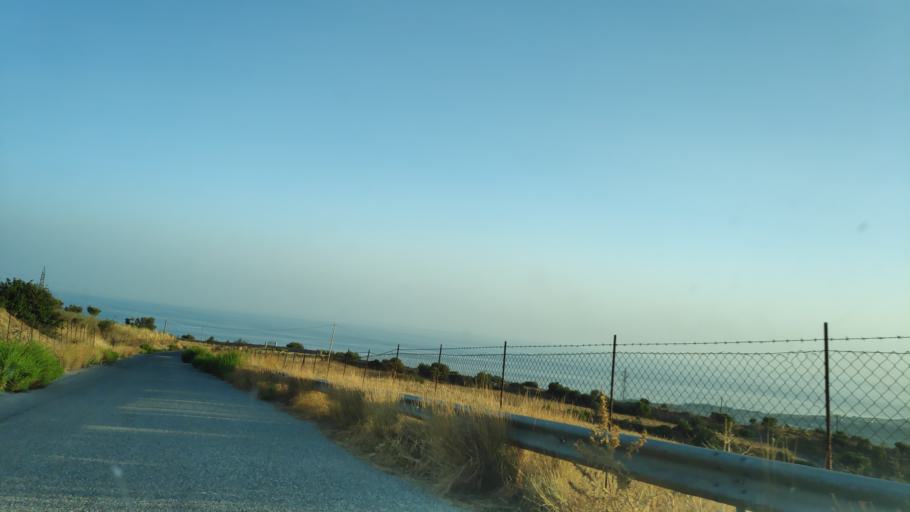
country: IT
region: Calabria
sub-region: Provincia di Reggio Calabria
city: Bova Marina
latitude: 37.9619
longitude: 15.9206
